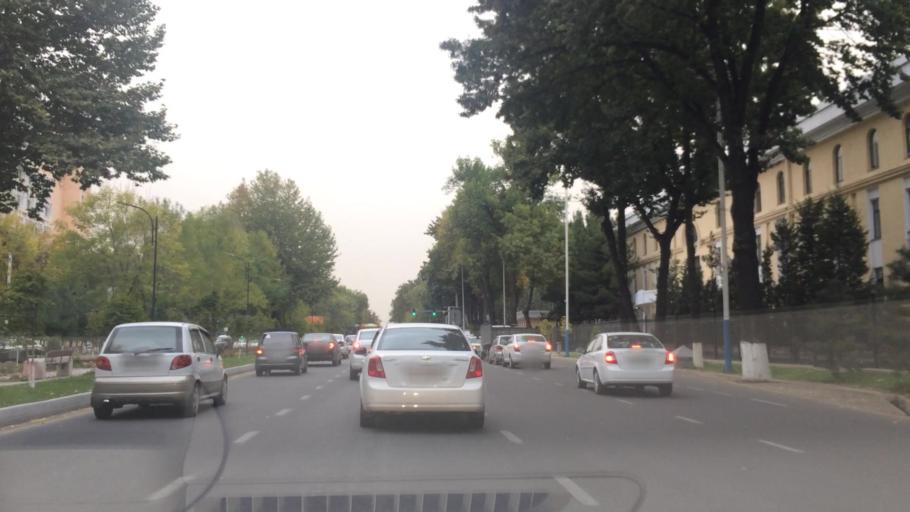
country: UZ
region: Toshkent Shahri
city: Tashkent
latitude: 41.3088
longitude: 69.2885
